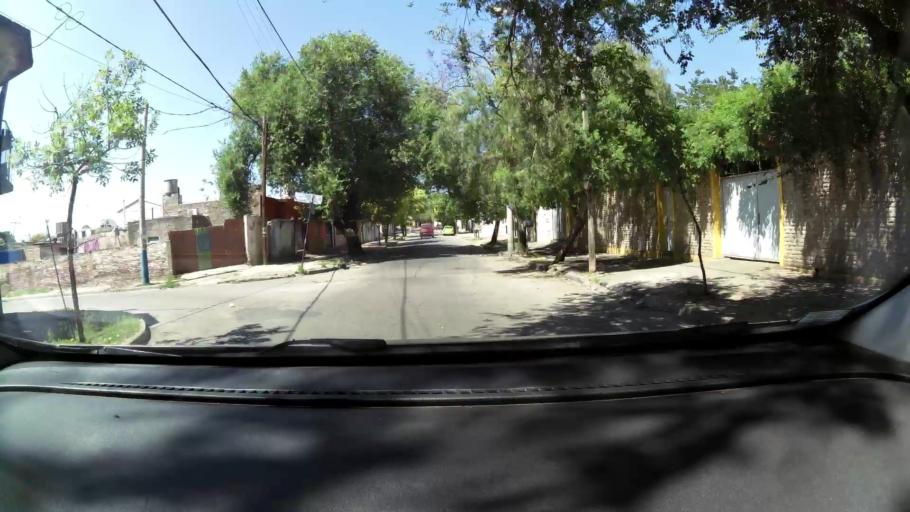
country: AR
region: Cordoba
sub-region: Departamento de Capital
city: Cordoba
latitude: -31.4248
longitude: -64.2037
